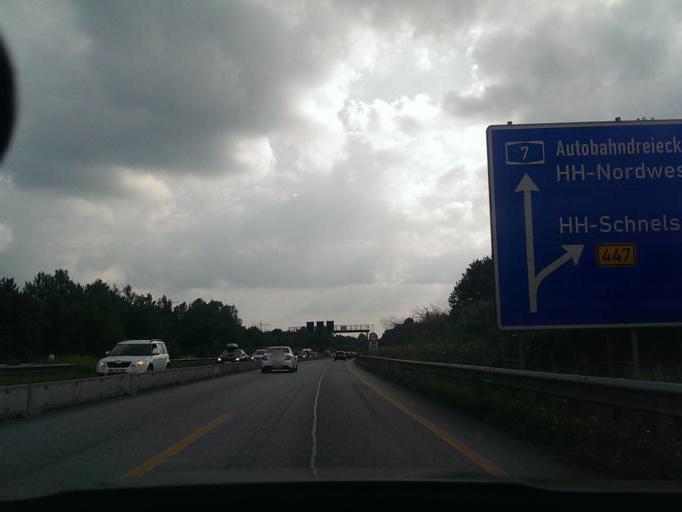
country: DE
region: Schleswig-Holstein
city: Bonningstedt
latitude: 53.6439
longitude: 9.9294
